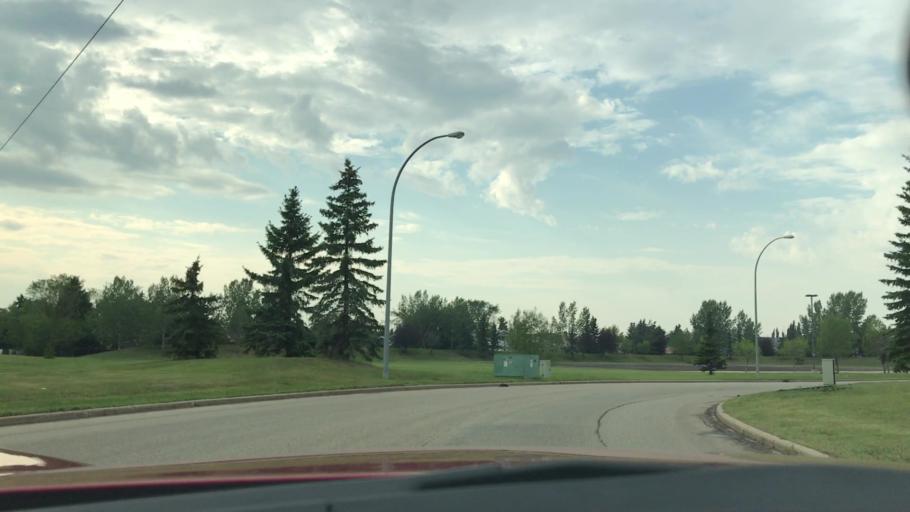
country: CA
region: Alberta
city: Edmonton
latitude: 53.4617
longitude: -113.4950
